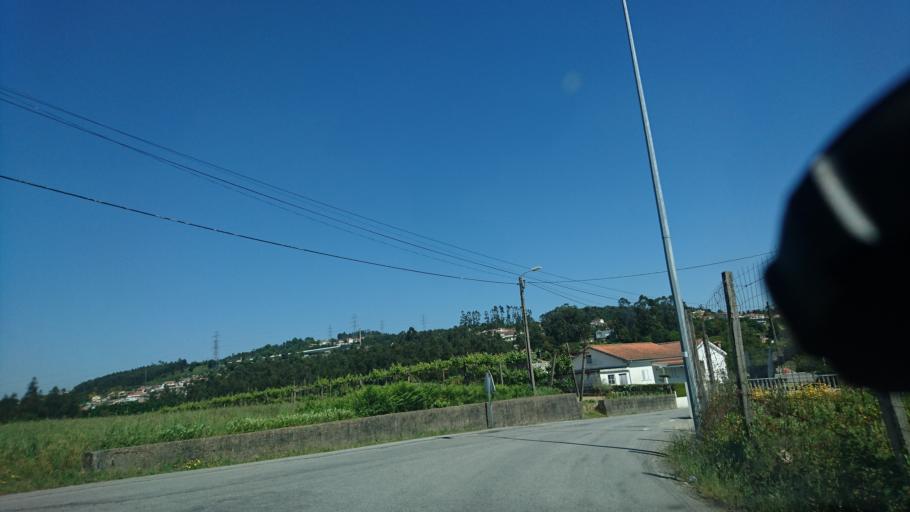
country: PT
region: Porto
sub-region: Paredes
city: Casteloes de Cepeda
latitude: 41.1824
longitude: -8.3407
